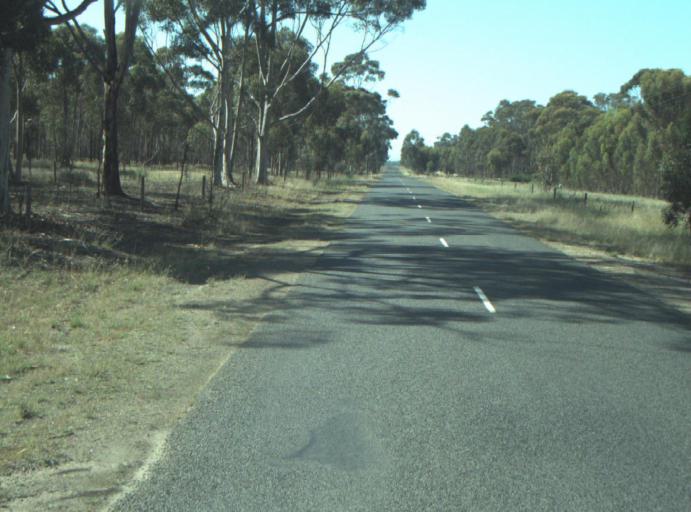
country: AU
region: Victoria
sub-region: Greater Geelong
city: Lara
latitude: -37.9585
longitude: 144.4010
